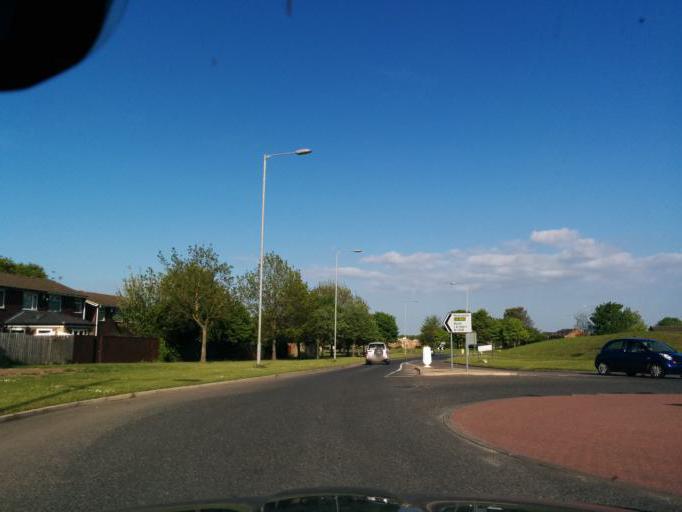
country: GB
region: England
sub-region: Northumberland
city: Cramlington
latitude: 55.0883
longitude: -1.5803
